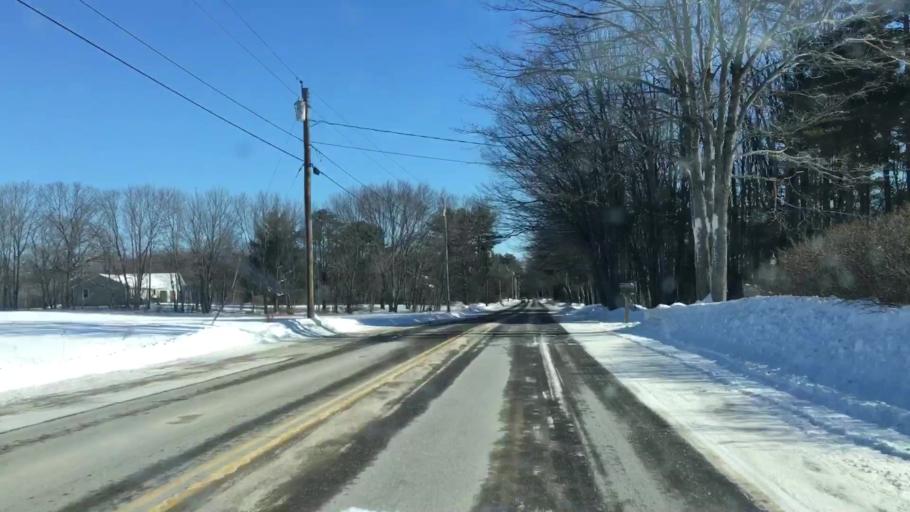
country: US
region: Maine
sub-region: Cumberland County
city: Brunswick
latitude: 43.8932
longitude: -69.9820
